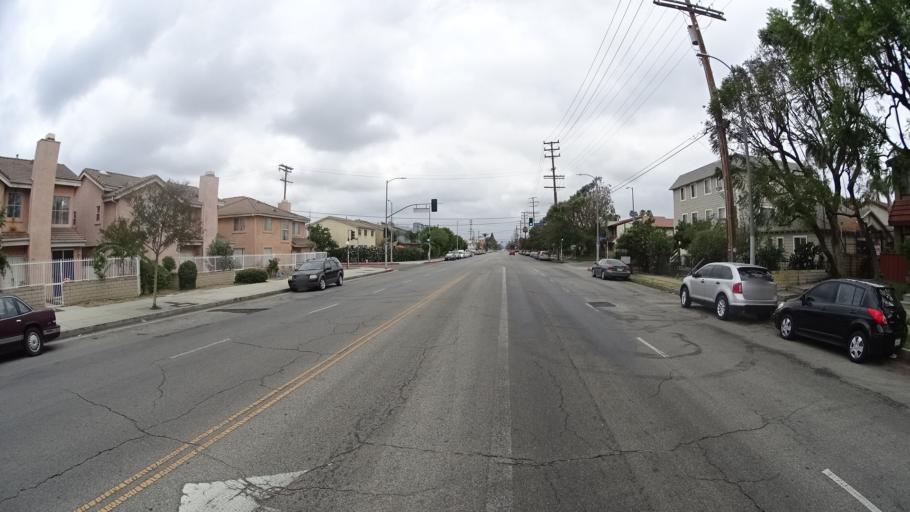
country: US
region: California
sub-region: Los Angeles County
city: San Fernando
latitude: 34.2427
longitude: -118.4475
